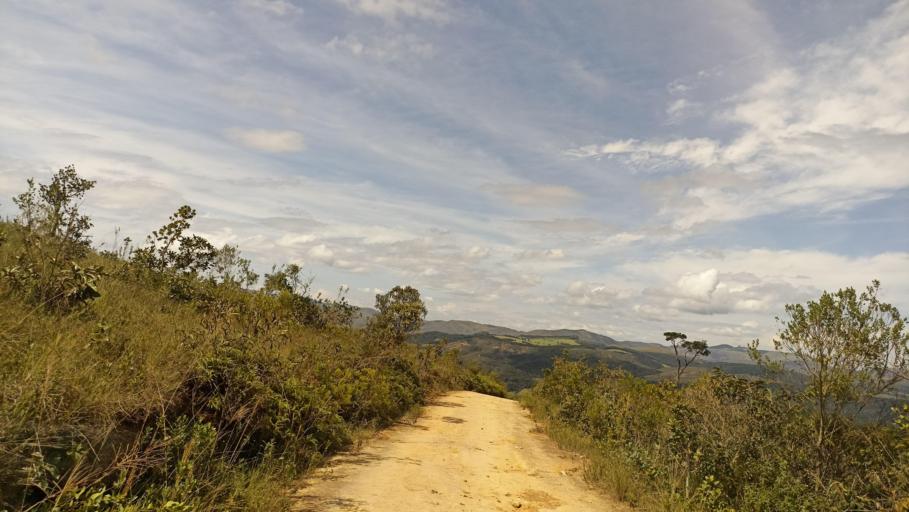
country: BR
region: Minas Gerais
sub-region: Itabirito
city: Itabirito
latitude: -20.3450
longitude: -43.7262
